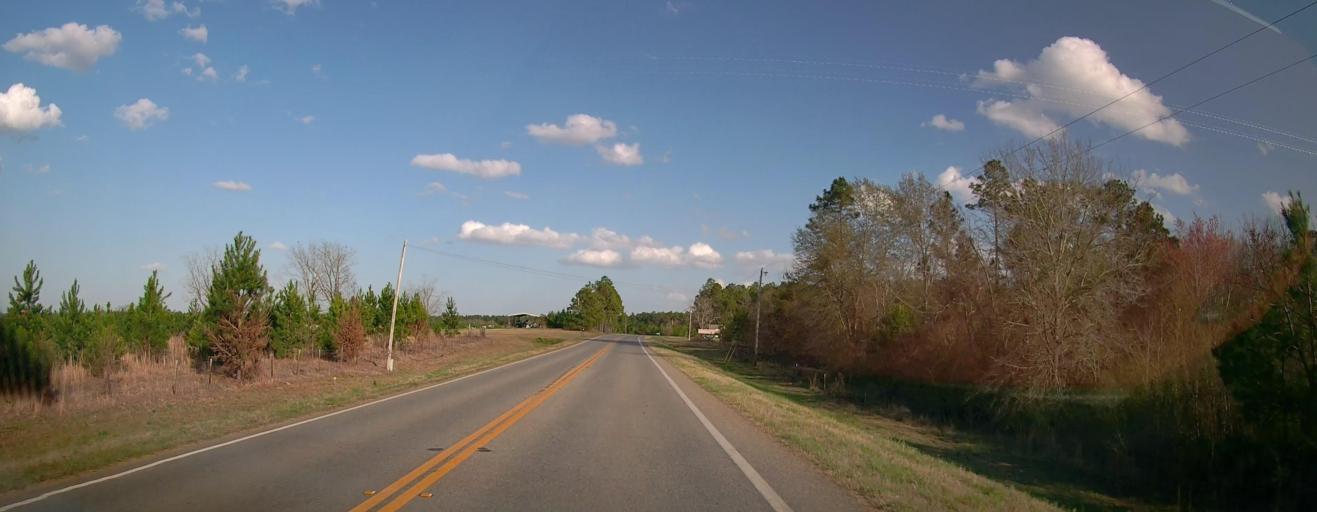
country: US
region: Georgia
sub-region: Toombs County
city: Lyons
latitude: 32.1749
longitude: -82.2815
